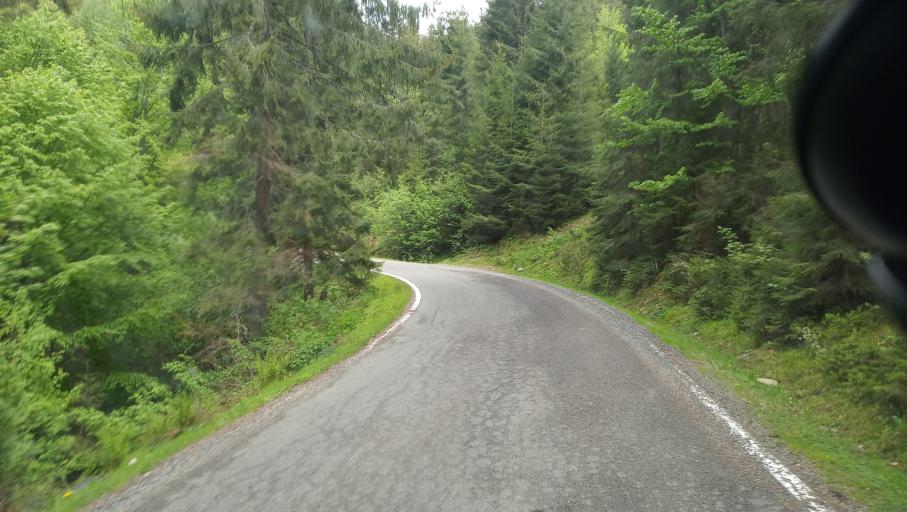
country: RO
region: Alba
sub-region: Comuna Horea
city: Horea
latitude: 46.5243
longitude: 22.8903
